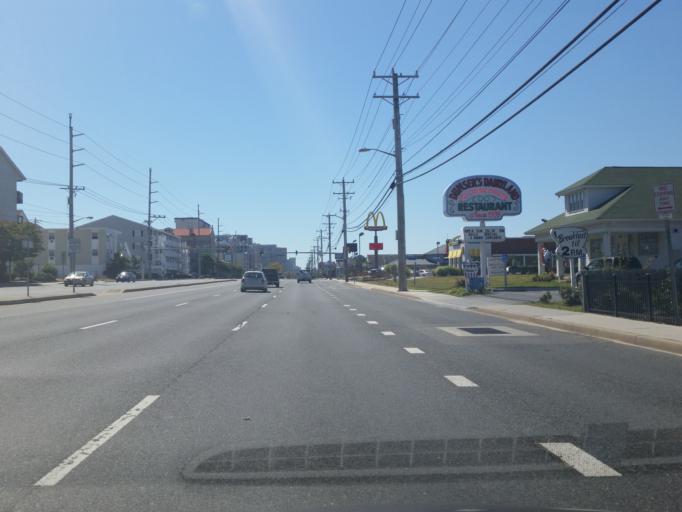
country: US
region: Maryland
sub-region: Worcester County
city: Ocean City
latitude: 38.4298
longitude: -75.0553
